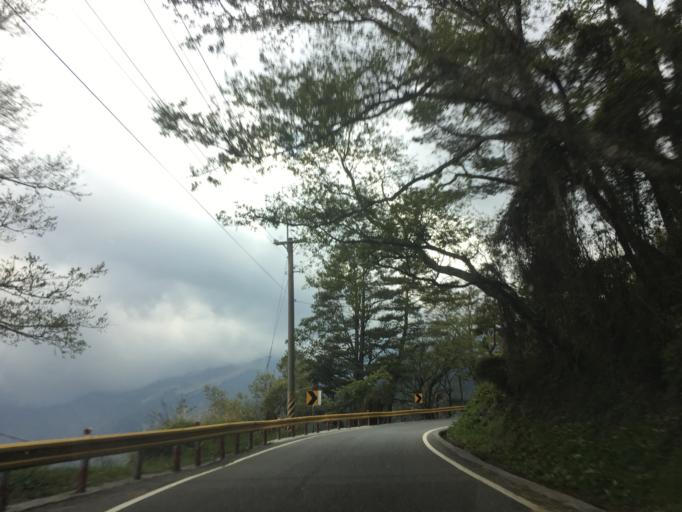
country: TW
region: Taiwan
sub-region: Hualien
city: Hualian
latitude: 24.1800
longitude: 121.3180
